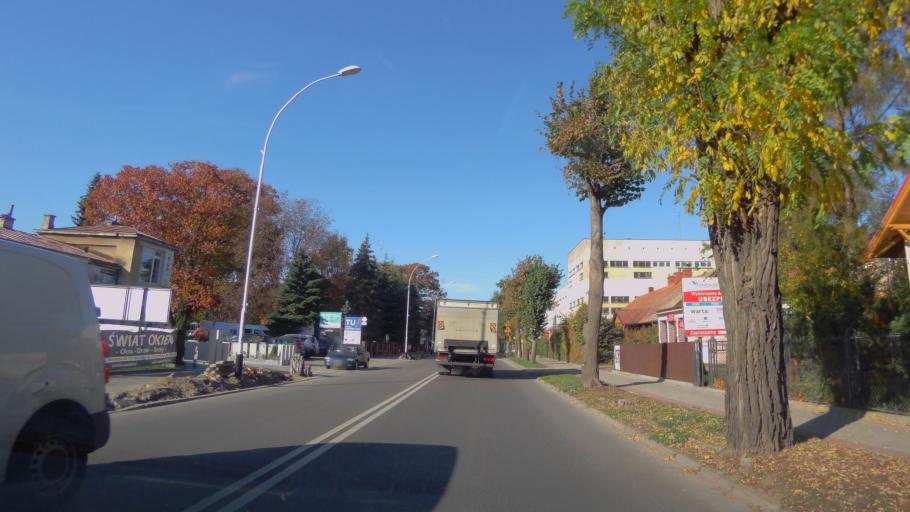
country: PL
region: Subcarpathian Voivodeship
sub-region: Powiat lezajski
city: Lezajsk
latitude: 50.2587
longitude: 22.4207
